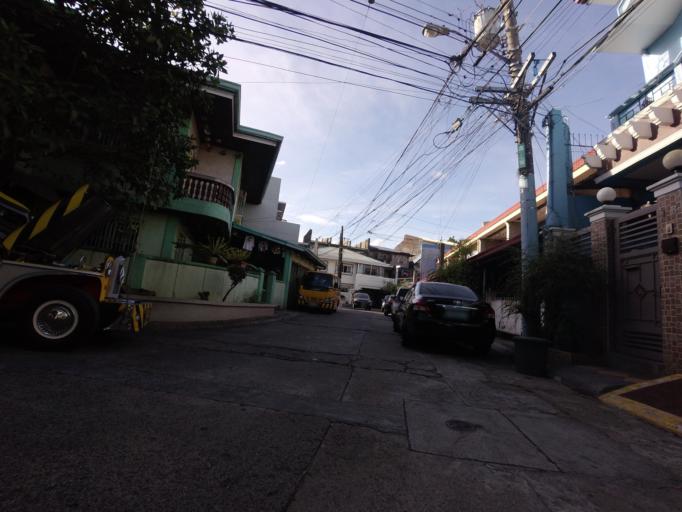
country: PH
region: Metro Manila
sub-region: Mandaluyong
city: Mandaluyong City
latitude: 14.5720
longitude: 121.0410
